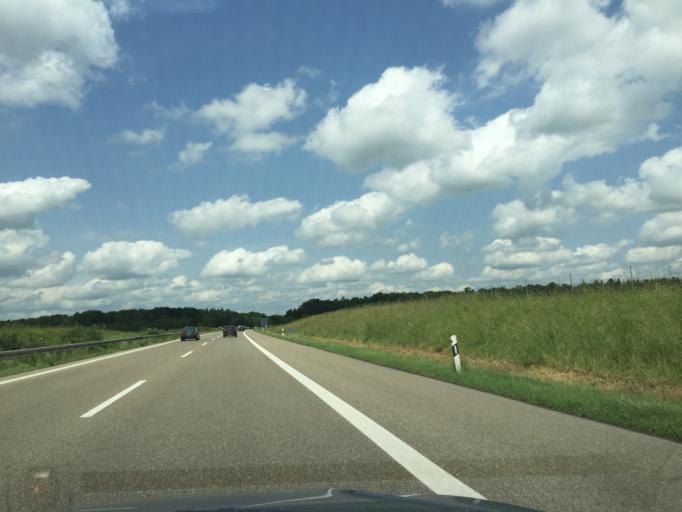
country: DE
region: Bavaria
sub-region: Swabia
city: Holzheim
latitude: 48.3531
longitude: 10.0827
